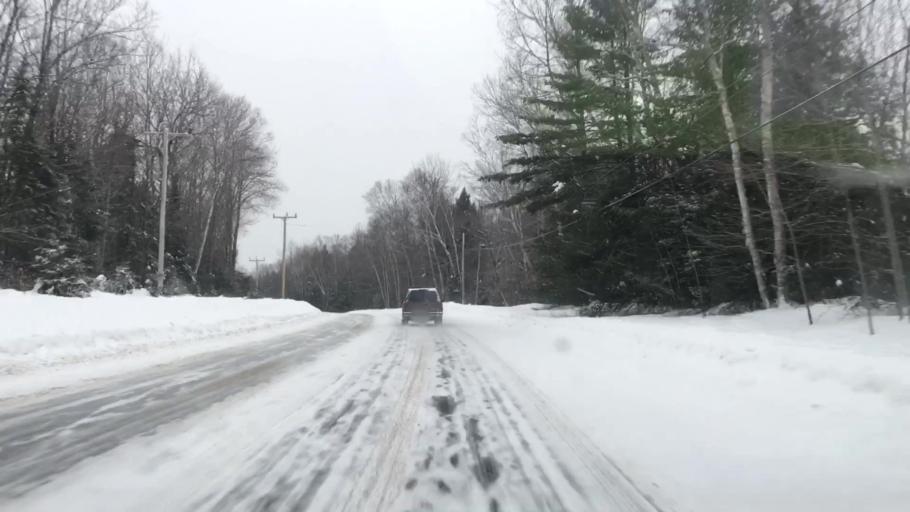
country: US
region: Maine
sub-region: Penobscot County
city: Medway
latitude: 45.5989
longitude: -68.4606
